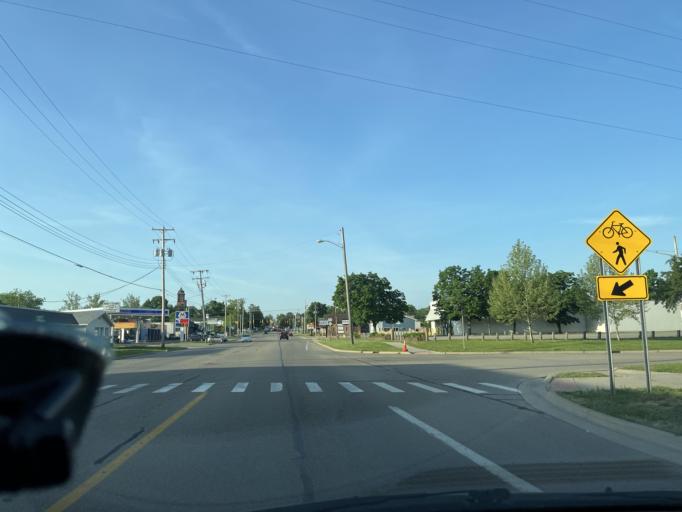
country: US
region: Michigan
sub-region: Barry County
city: Hastings
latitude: 42.6517
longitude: -85.2907
